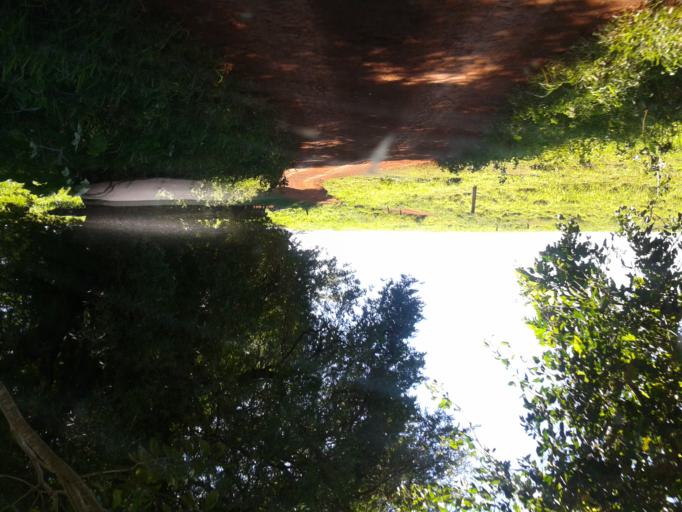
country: BR
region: Minas Gerais
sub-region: Capinopolis
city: Capinopolis
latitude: -18.6287
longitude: -49.6130
